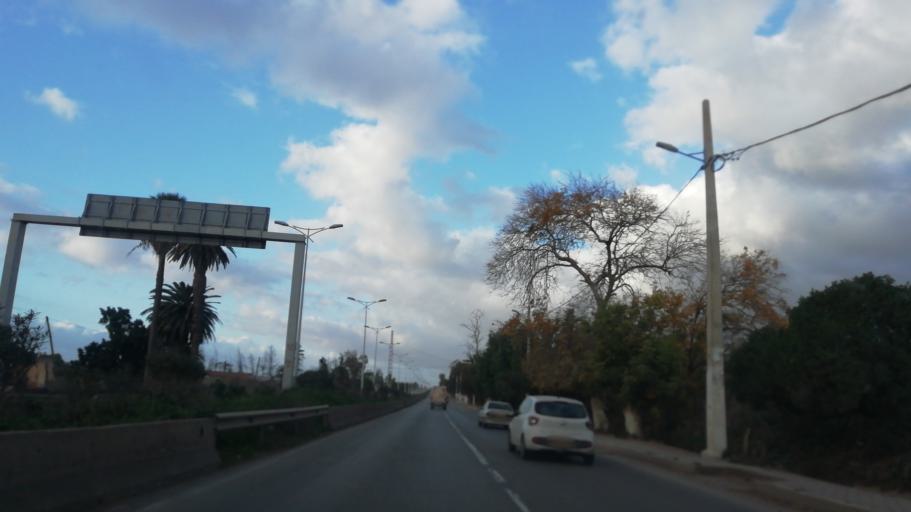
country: DZ
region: Oran
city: Bou Tlelis
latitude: 35.5762
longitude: -0.8483
